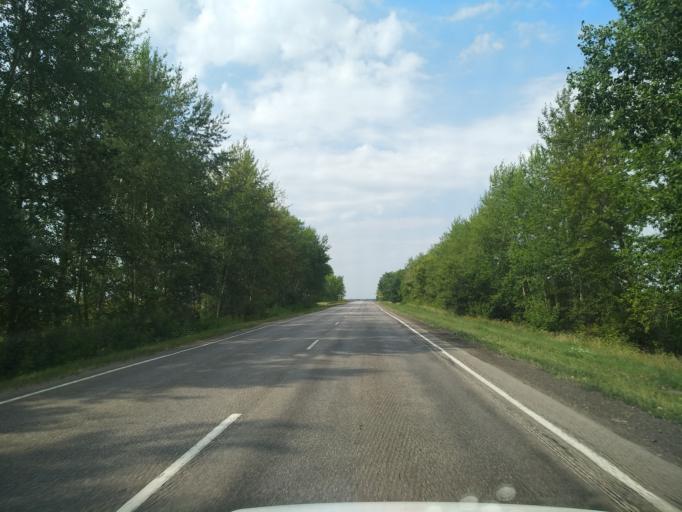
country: RU
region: Voronezj
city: Verkhnyaya Khava
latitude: 51.6953
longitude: 39.9521
